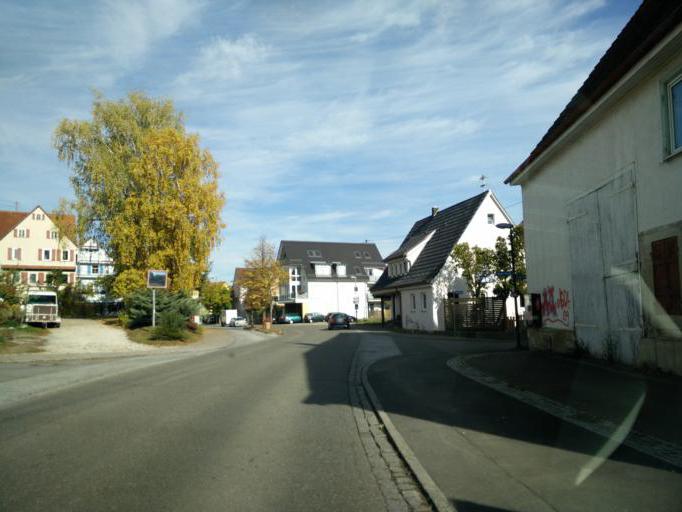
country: DE
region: Baden-Wuerttemberg
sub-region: Tuebingen Region
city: Kusterdingen
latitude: 48.4972
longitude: 9.1015
